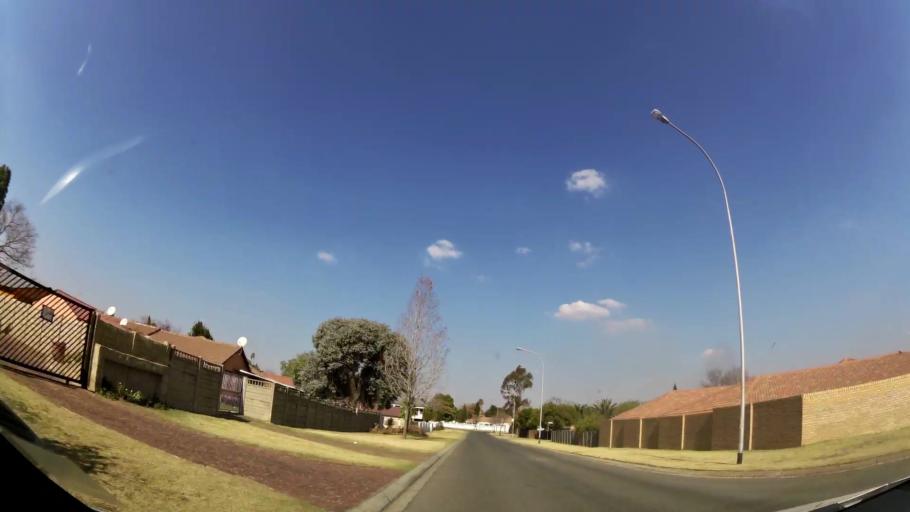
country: ZA
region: Gauteng
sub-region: Ekurhuleni Metropolitan Municipality
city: Benoni
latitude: -26.2441
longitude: 28.3113
